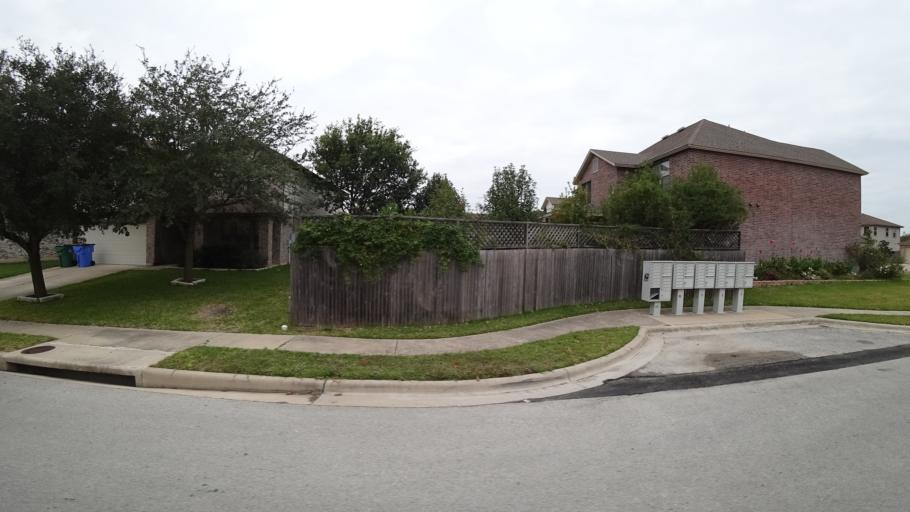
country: US
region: Texas
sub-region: Travis County
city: Pflugerville
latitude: 30.4564
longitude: -97.6212
